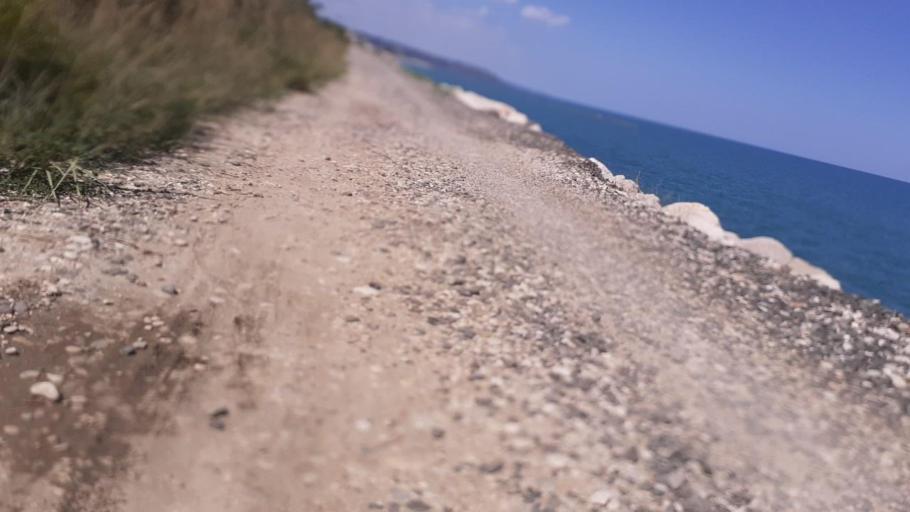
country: IT
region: Abruzzo
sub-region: Provincia di Chieti
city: Torino di Sangro
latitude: 42.2222
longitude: 14.5659
